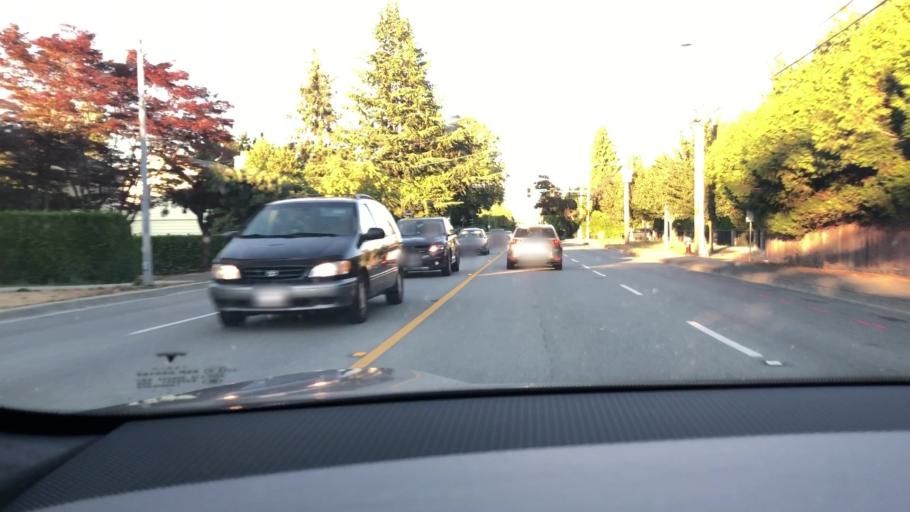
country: CA
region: British Columbia
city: Richmond
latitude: 49.1556
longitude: -123.1493
